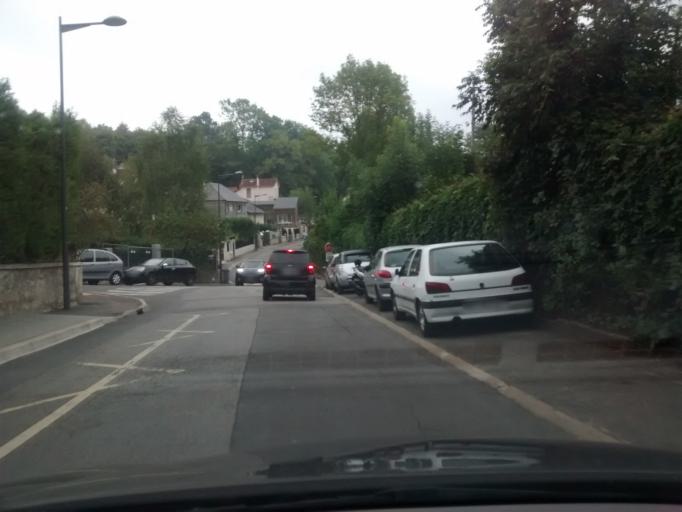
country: FR
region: Ile-de-France
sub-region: Departement des Hauts-de-Seine
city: Ville-d'Avray
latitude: 48.8156
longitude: 2.1906
